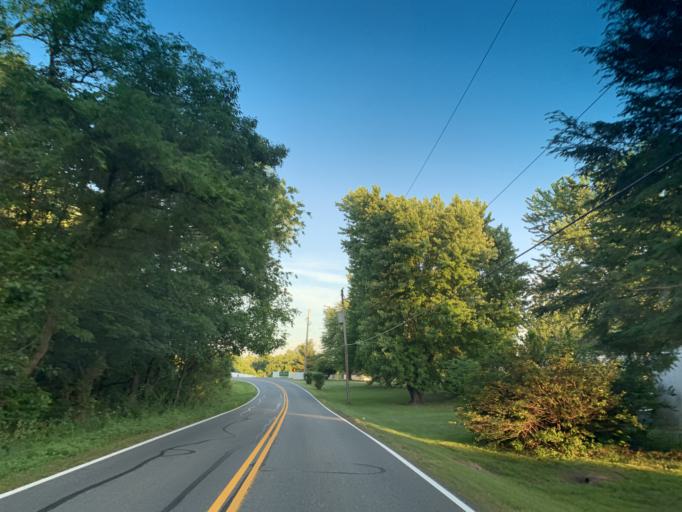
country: US
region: Maryland
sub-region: Cecil County
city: Perryville
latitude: 39.6285
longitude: -76.0673
